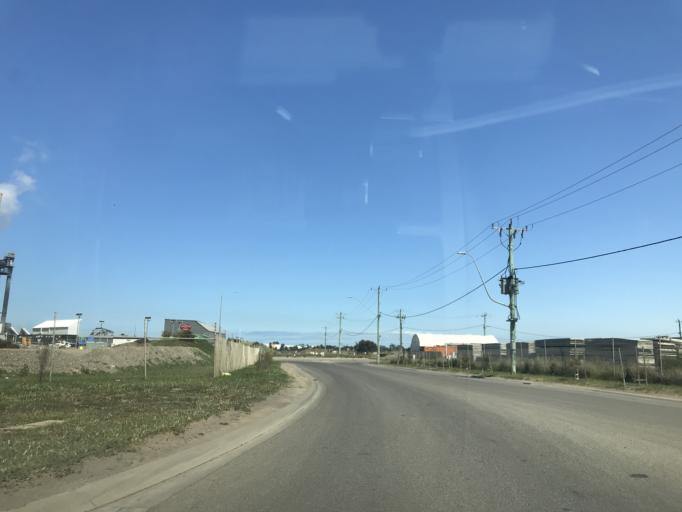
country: AU
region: Victoria
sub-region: Wyndham
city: Truganina
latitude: -37.8294
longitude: 144.7702
